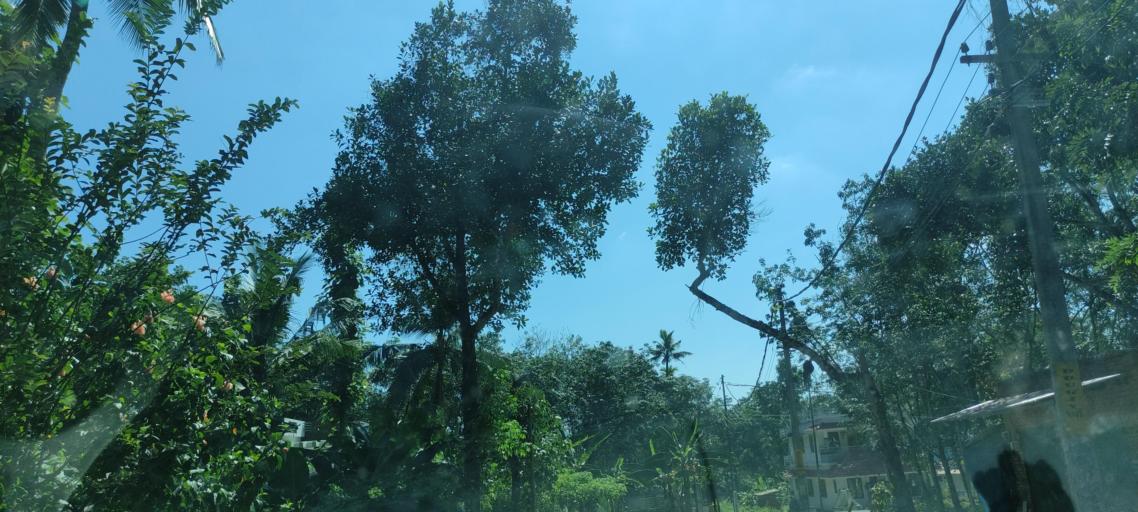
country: IN
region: Kerala
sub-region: Pattanamtitta
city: Adur
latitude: 9.0951
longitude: 76.7366
